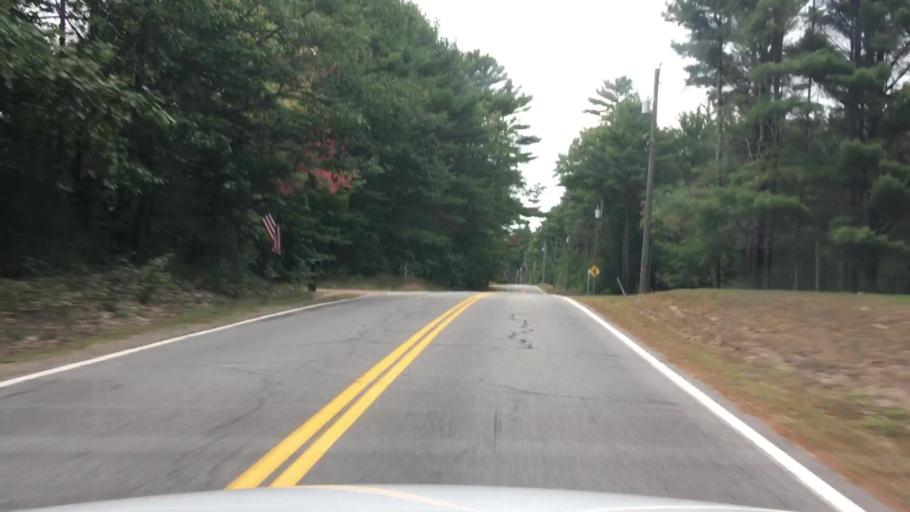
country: US
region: New Hampshire
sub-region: Carroll County
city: Effingham
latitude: 43.7133
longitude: -70.9847
